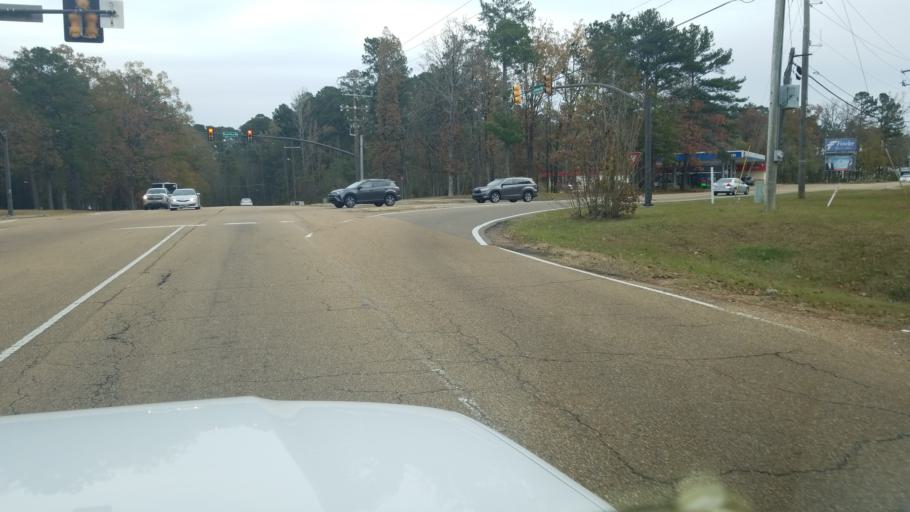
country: US
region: Mississippi
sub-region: Rankin County
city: Brandon
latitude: 32.3727
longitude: -90.0176
